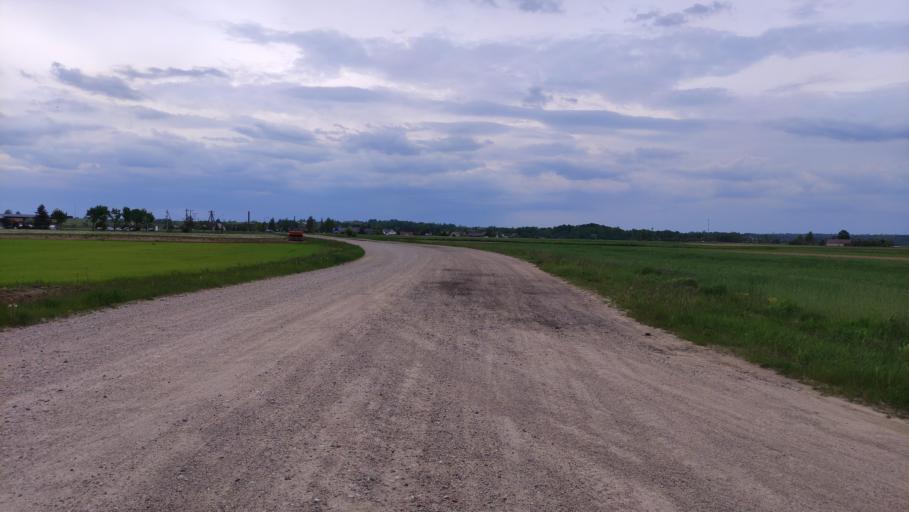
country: LT
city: Prienai
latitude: 54.5094
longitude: 23.9144
